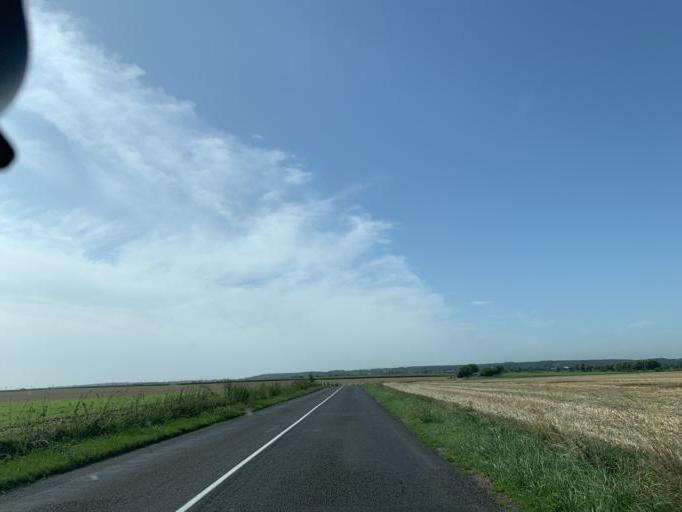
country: FR
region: Ile-de-France
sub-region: Departement de Seine-et-Marne
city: Claye-Souilly
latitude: 48.9618
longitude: 2.6987
